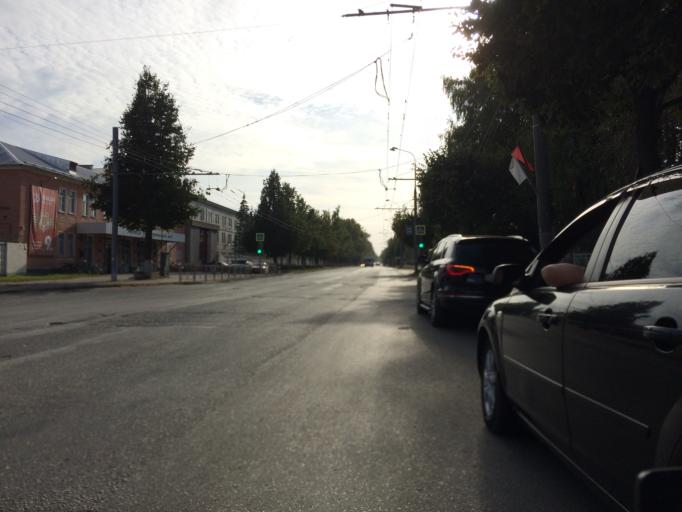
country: RU
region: Mariy-El
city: Yoshkar-Ola
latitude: 56.6338
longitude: 47.8575
